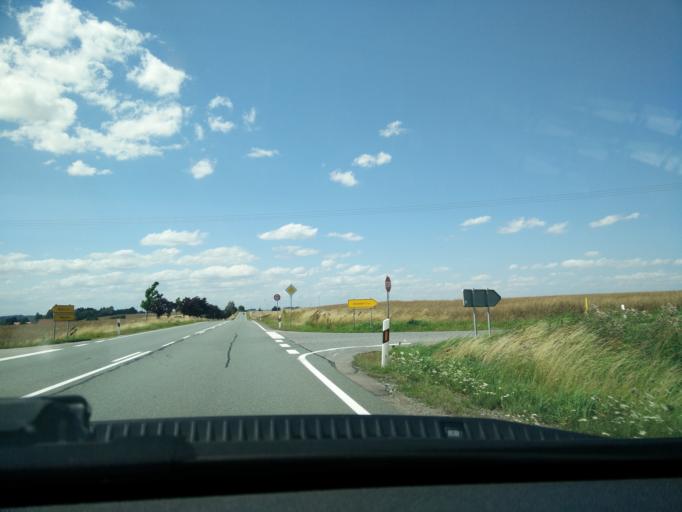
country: DE
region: Saxony
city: Niederfrohna
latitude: 50.9143
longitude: 12.7341
